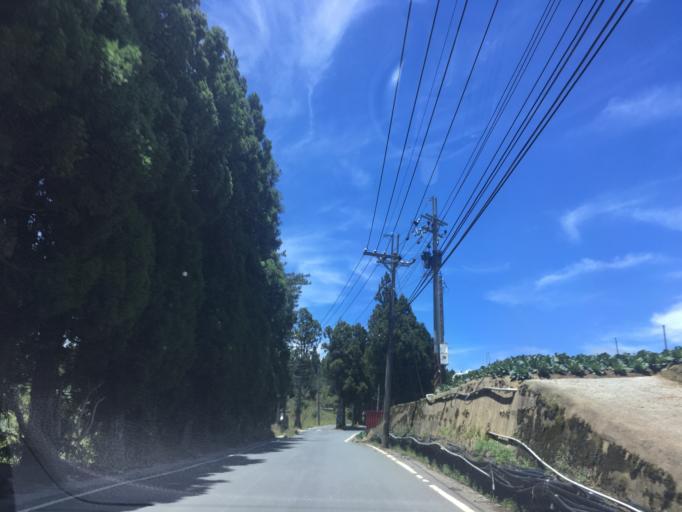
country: TW
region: Taiwan
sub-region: Nantou
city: Puli
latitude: 24.2394
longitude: 121.2457
